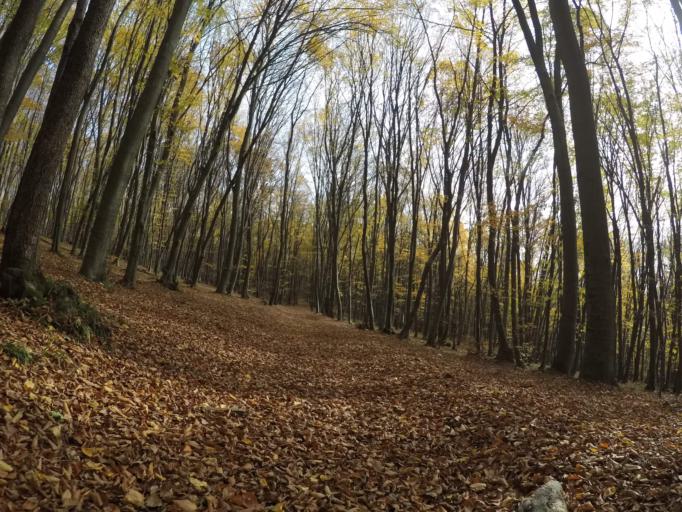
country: SK
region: Presovsky
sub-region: Okres Presov
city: Presov
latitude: 48.9205
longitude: 21.2239
